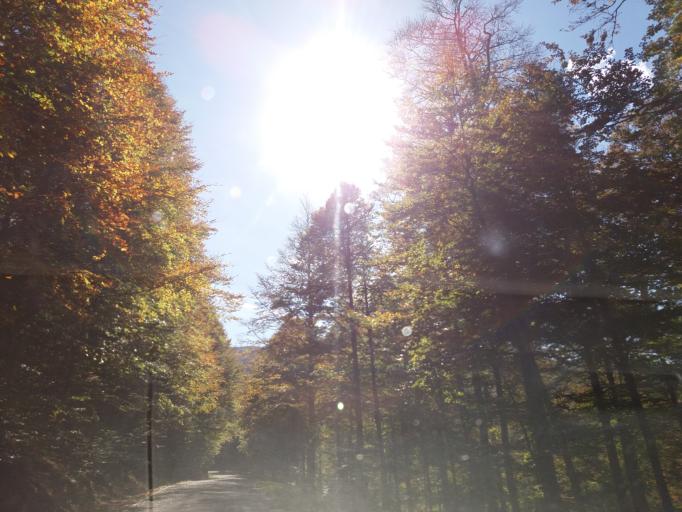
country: ES
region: Navarre
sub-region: Provincia de Navarra
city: Oronz
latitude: 42.9707
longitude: -1.1235
